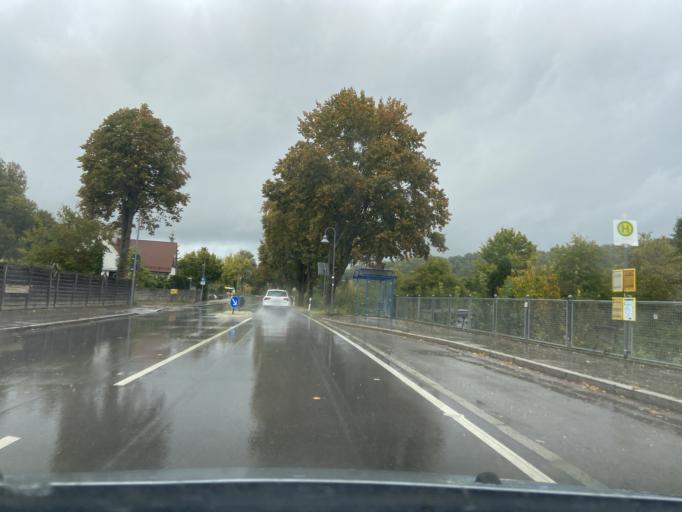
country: DE
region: Baden-Wuerttemberg
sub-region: Tuebingen Region
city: Sigmaringendorf
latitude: 48.0779
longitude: 9.2723
